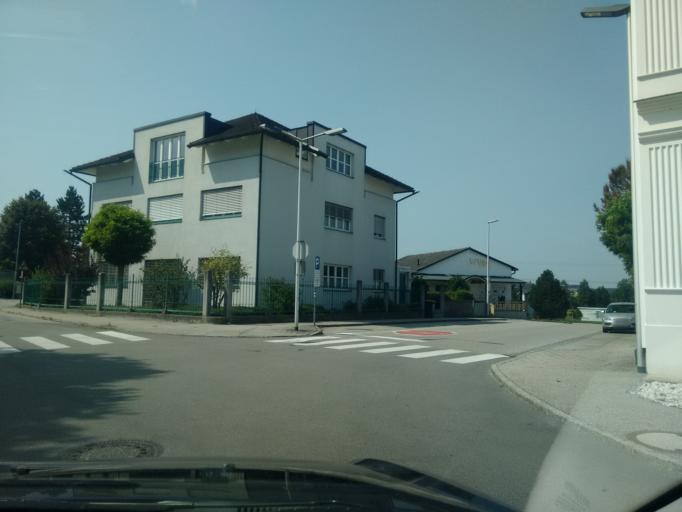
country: AT
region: Upper Austria
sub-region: Wels-Land
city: Gunskirchen
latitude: 48.1332
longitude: 13.9409
